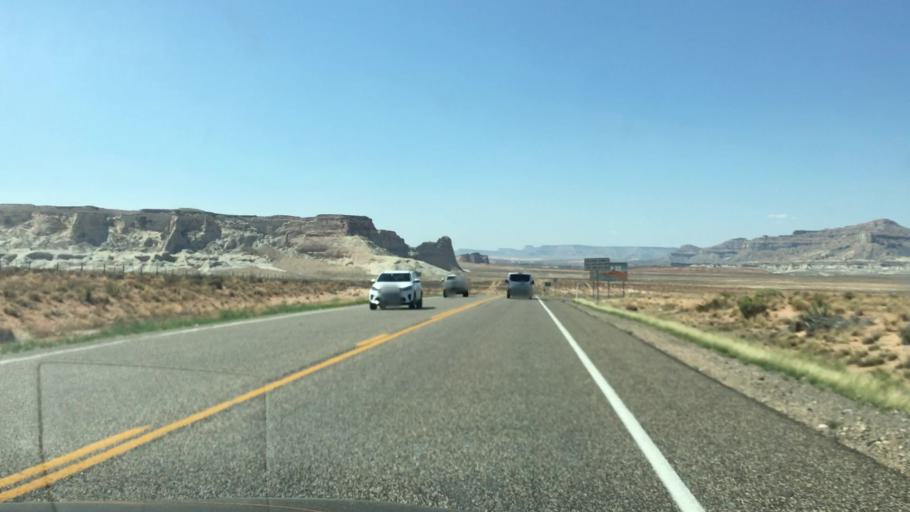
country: US
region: Arizona
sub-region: Coconino County
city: Page
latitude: 37.0017
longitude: -111.5728
